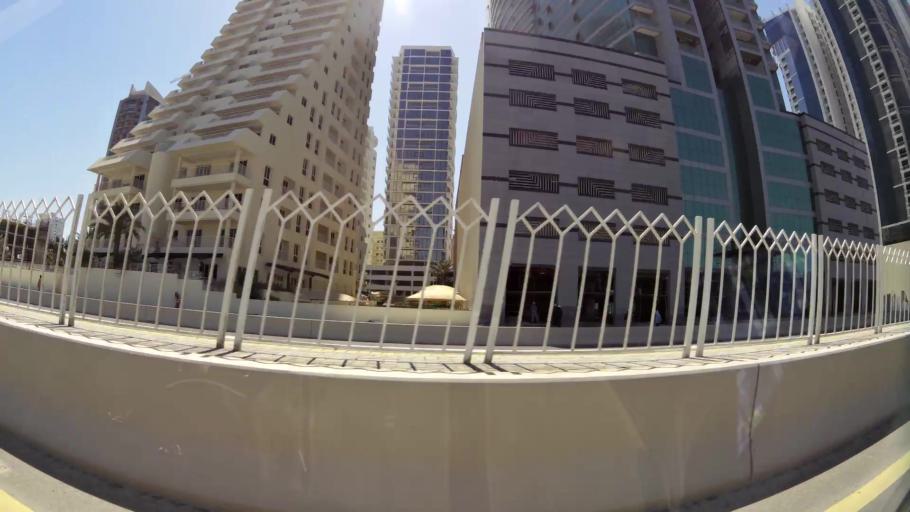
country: BH
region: Manama
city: Manama
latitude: 26.2245
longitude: 50.6099
